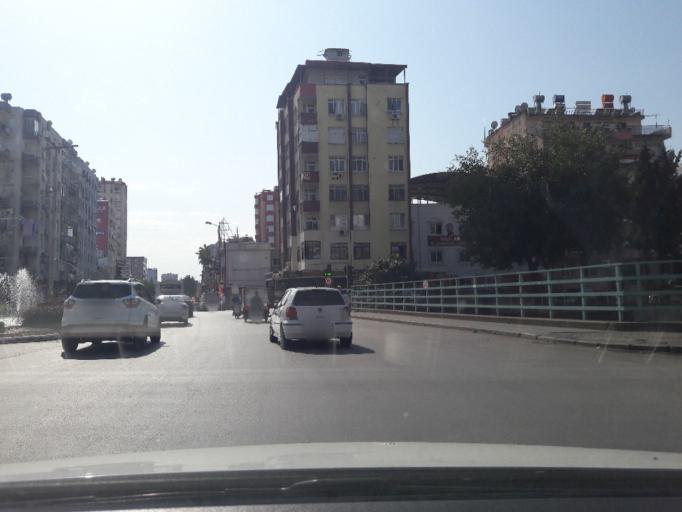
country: TR
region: Adana
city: Adana
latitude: 37.0095
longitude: 35.3237
